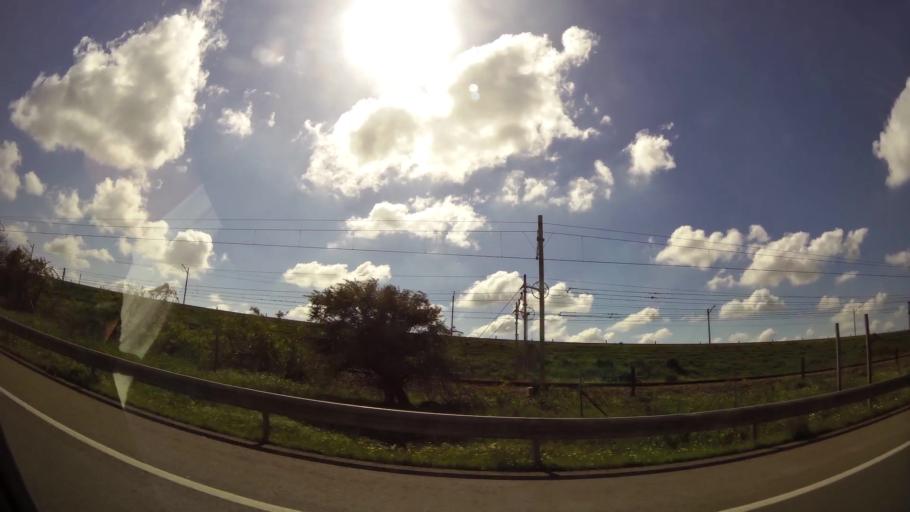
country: MA
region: Chaouia-Ouardigha
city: Nouaseur
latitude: 33.4107
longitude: -7.6264
